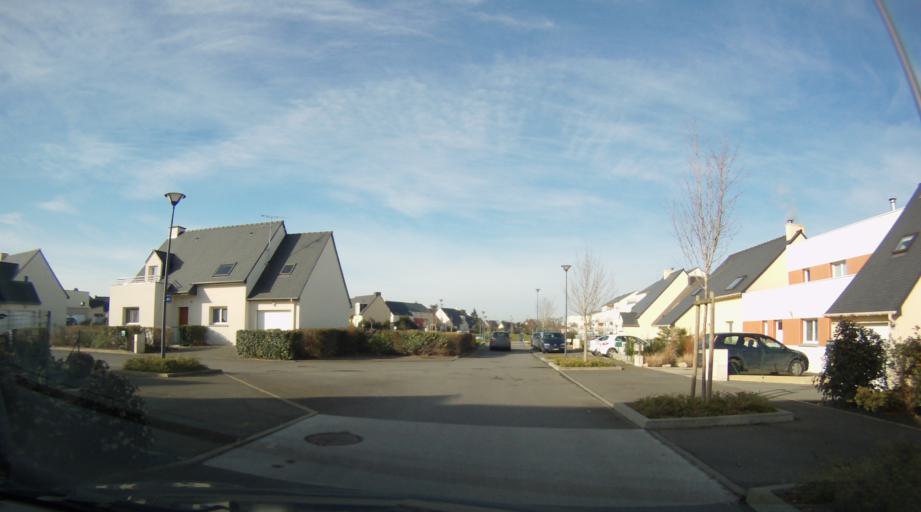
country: FR
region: Brittany
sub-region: Departement d'Ille-et-Vilaine
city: Bourgbarre
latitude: 47.9917
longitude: -1.6064
